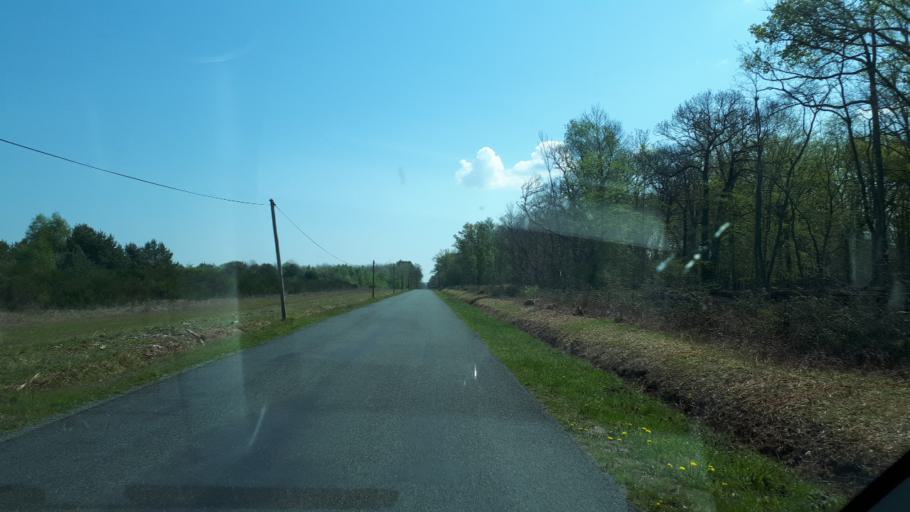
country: FR
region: Centre
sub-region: Departement du Cher
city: Neuvy-sur-Barangeon
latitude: 47.3189
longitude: 2.2103
